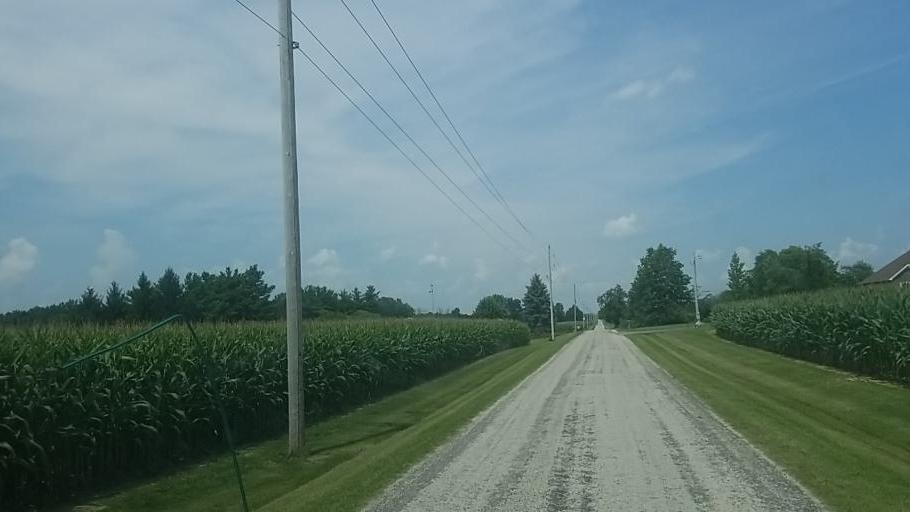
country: US
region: Ohio
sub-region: Wyandot County
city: Upper Sandusky
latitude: 40.6496
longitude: -83.3619
